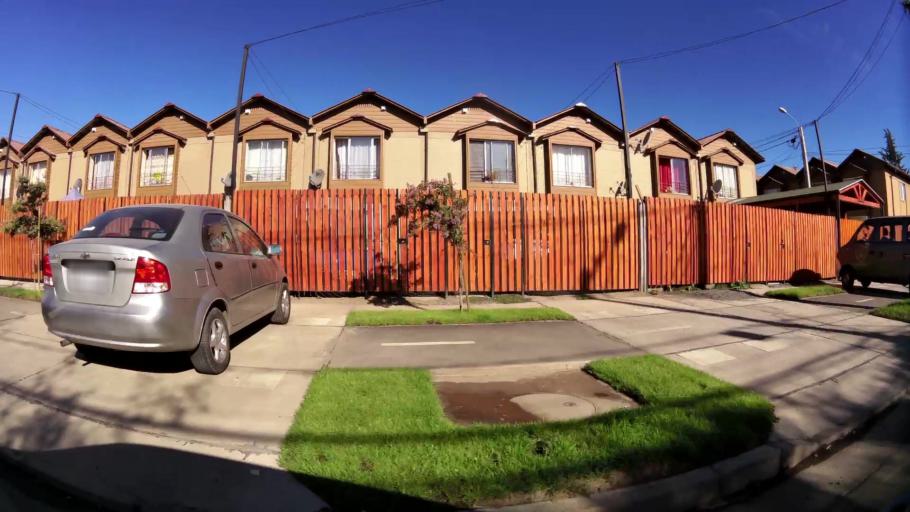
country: CL
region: O'Higgins
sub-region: Provincia de Cachapoal
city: Rancagua
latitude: -34.1785
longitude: -70.7554
